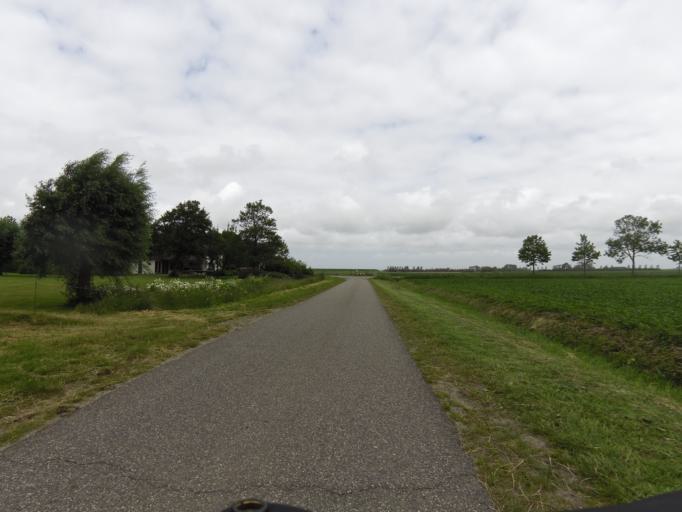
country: NL
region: Zeeland
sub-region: Schouwen-Duiveland
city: Bruinisse
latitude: 51.6322
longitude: 3.9604
